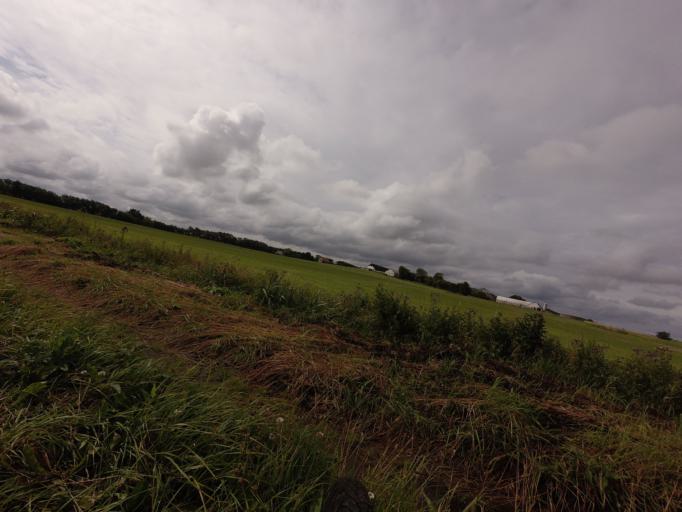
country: DK
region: North Denmark
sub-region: Jammerbugt Kommune
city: Pandrup
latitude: 57.3159
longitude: 9.7426
